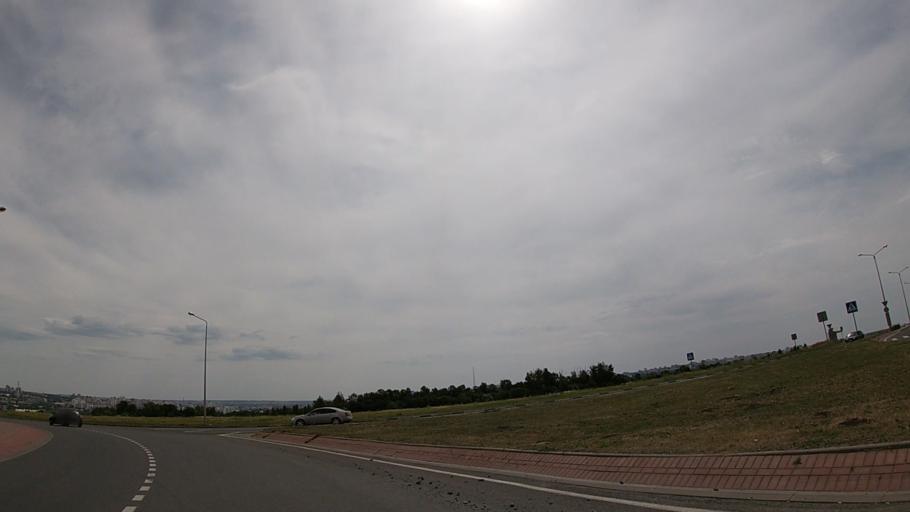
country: RU
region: Belgorod
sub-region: Belgorodskiy Rayon
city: Belgorod
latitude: 50.5930
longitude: 36.5308
